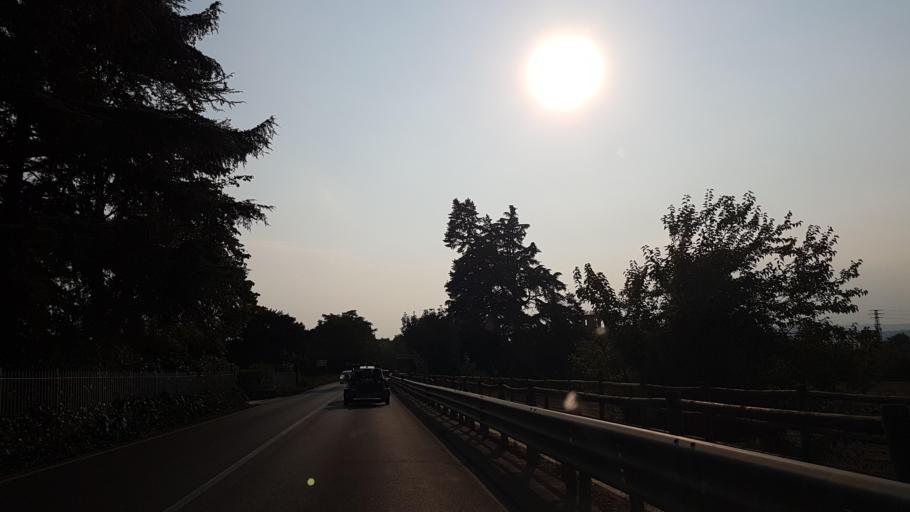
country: IT
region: Emilia-Romagna
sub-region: Provincia di Parma
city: Ozzano Taro
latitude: 44.7141
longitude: 10.1469
